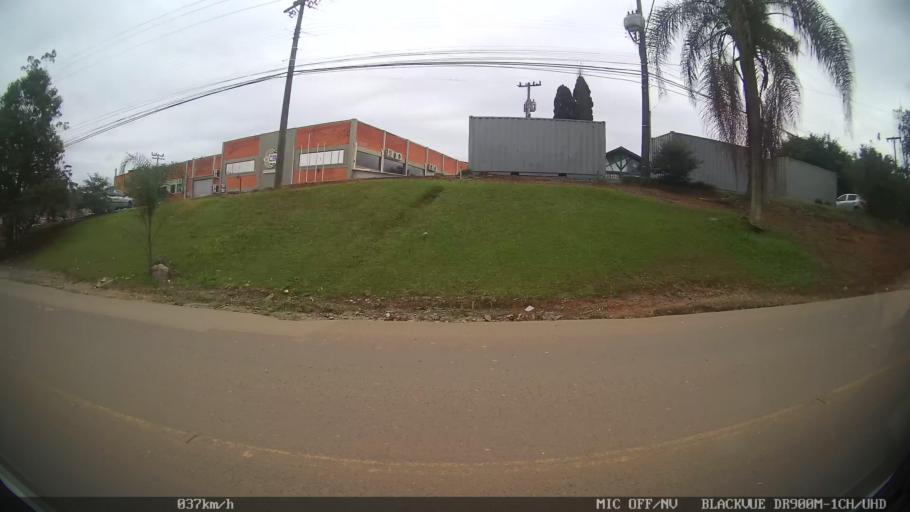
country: BR
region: Santa Catarina
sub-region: Joinville
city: Joinville
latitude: -26.2598
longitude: -48.8832
